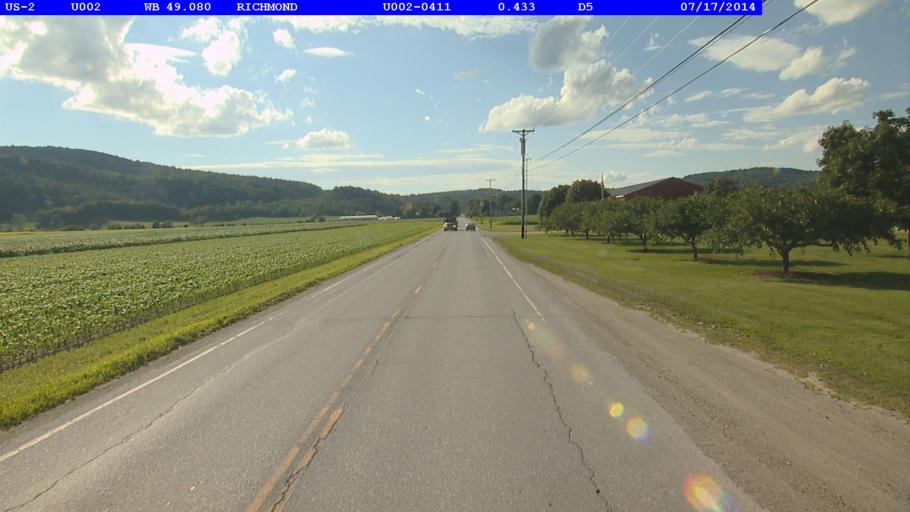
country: US
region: Vermont
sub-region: Chittenden County
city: Williston
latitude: 44.4252
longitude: -73.0215
